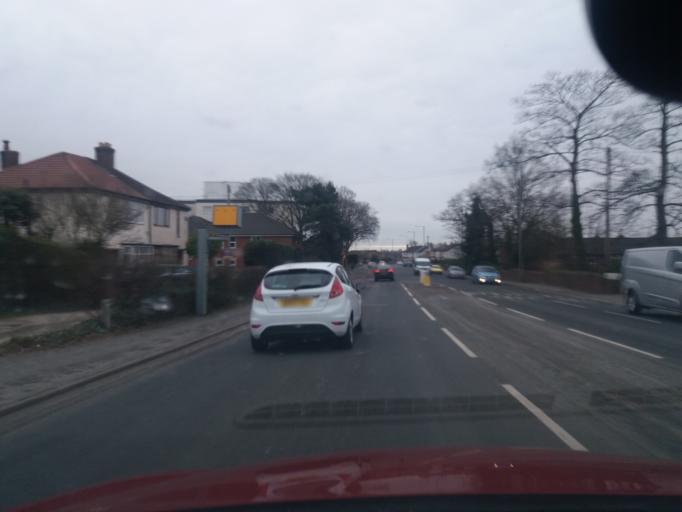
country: GB
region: England
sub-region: Lancashire
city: Chorley
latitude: 53.6651
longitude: -2.6323
